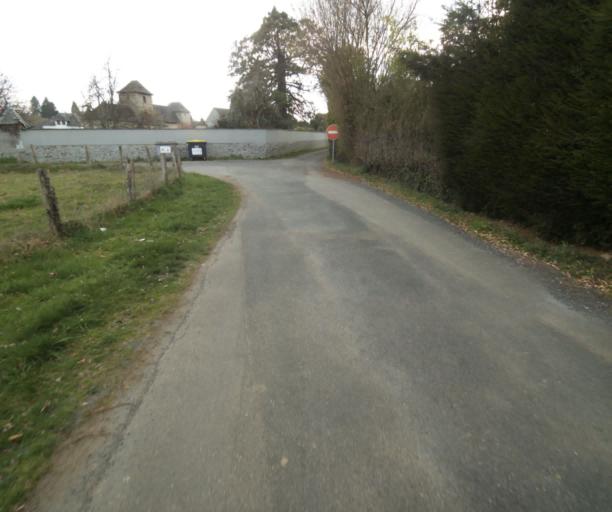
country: FR
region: Limousin
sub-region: Departement de la Correze
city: Saint-Clement
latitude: 45.3538
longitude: 1.6401
